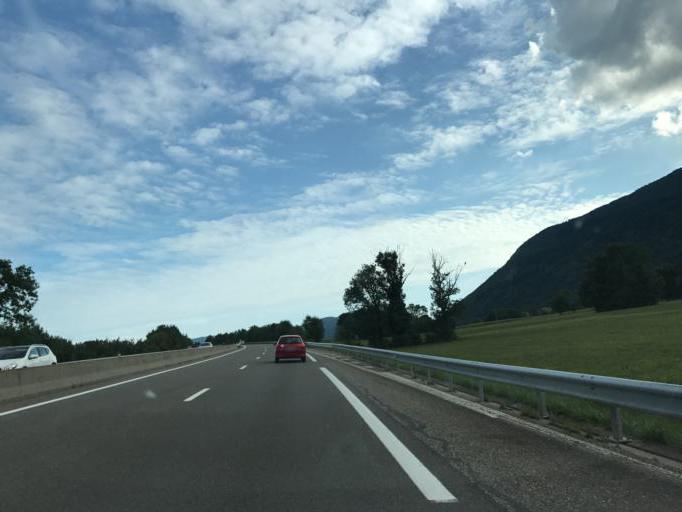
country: FR
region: Rhone-Alpes
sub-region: Departement de l'Ain
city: Collonges
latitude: 46.1568
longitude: 5.9090
